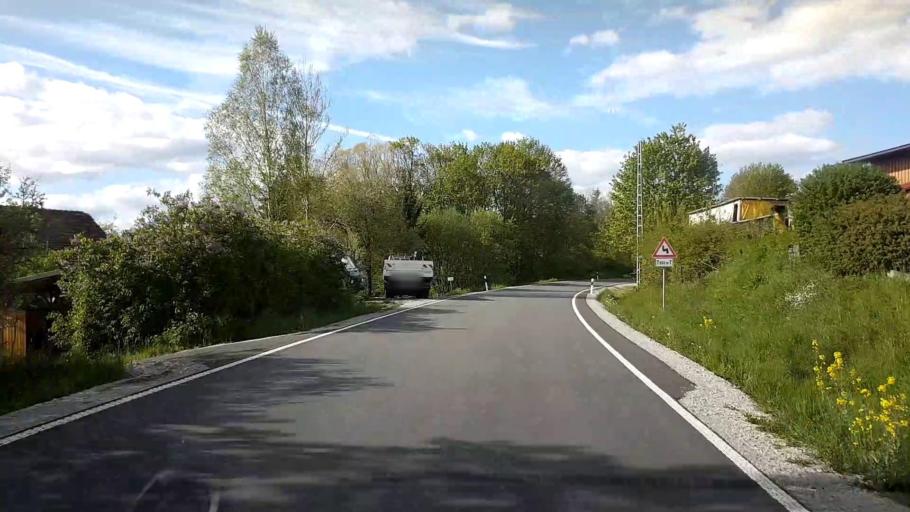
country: DE
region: Bavaria
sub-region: Upper Franconia
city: Hollfeld
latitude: 49.9434
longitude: 11.2828
